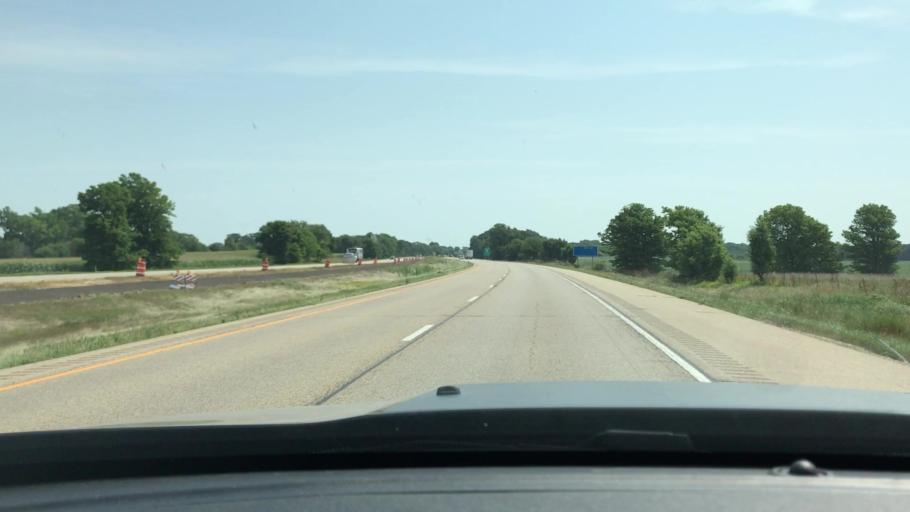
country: US
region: Illinois
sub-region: Bureau County
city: Walnut
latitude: 41.3855
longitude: -89.7156
